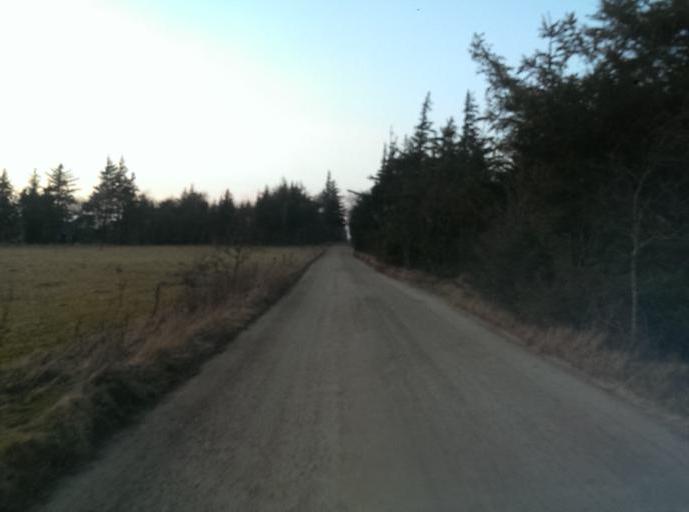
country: DK
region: South Denmark
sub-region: Varde Kommune
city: Oksbol
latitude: 55.5602
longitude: 8.3157
